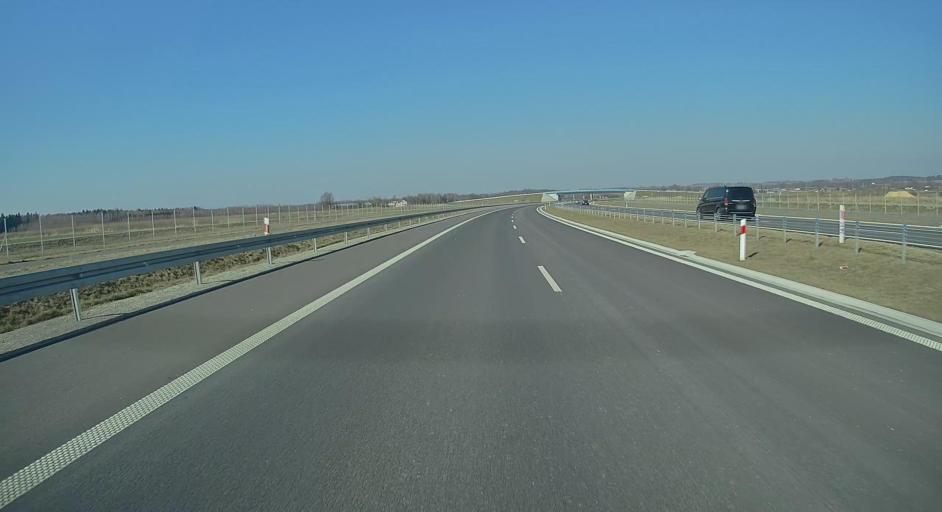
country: PL
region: Lublin Voivodeship
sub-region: Powiat janowski
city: Modliborzyce
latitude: 50.7439
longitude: 22.3032
